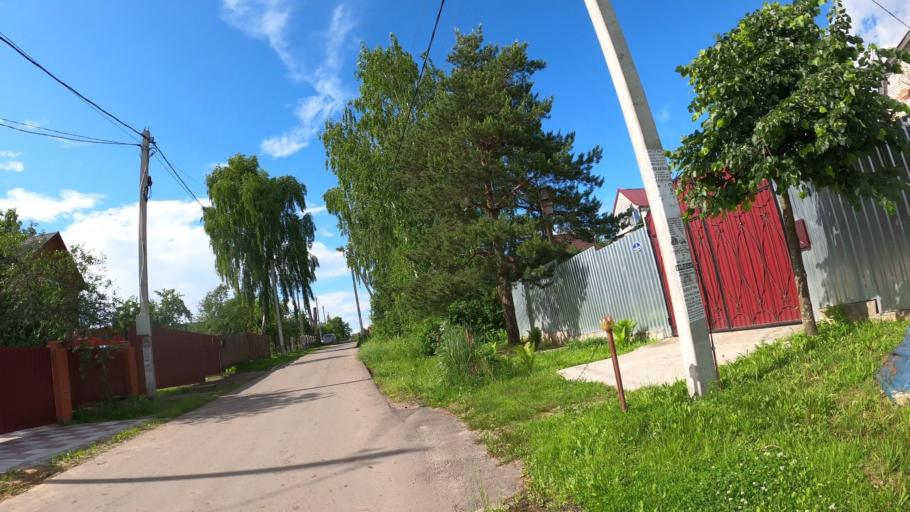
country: RU
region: Moskovskaya
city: Konobeyevo
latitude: 55.4163
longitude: 38.6517
